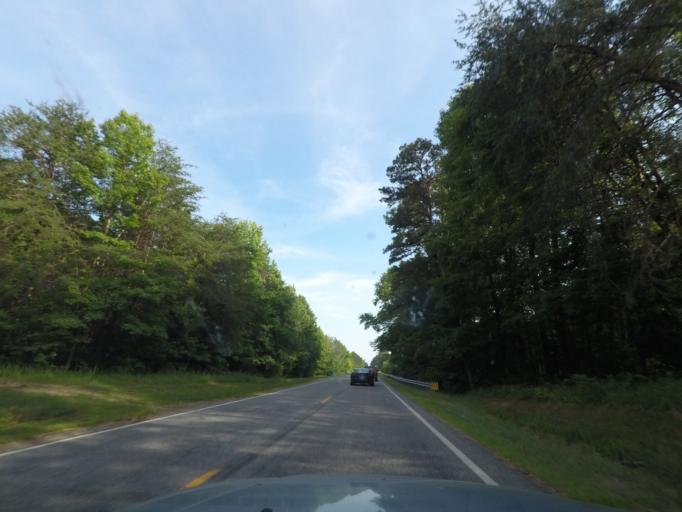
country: US
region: Virginia
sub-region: Mecklenburg County
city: Clarksville
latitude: 36.5607
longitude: -78.5423
